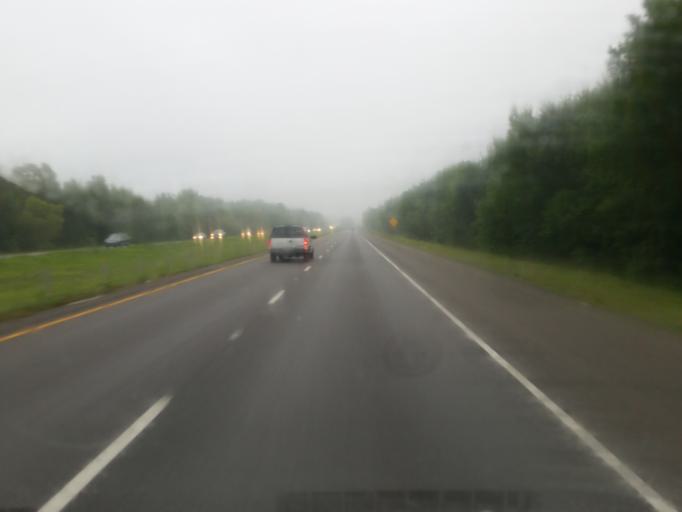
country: US
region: Louisiana
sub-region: Bossier Parish
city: Eastwood
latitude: 32.5419
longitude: -93.5865
